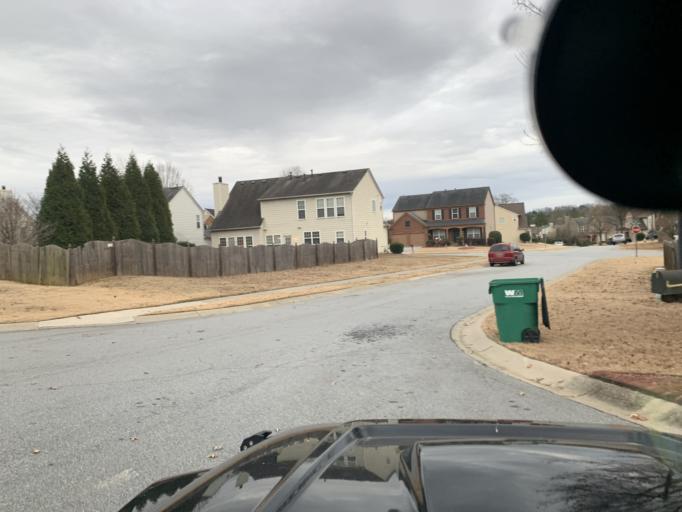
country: US
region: Georgia
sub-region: Cherokee County
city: Woodstock
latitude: 34.0965
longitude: -84.4603
